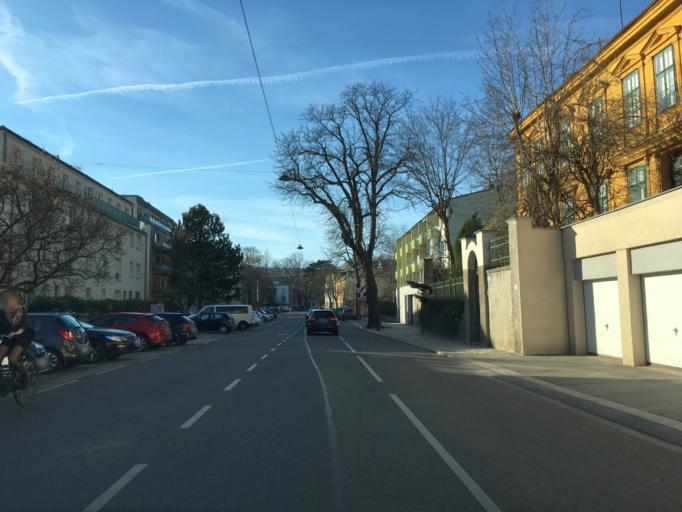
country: AT
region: Lower Austria
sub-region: Politischer Bezirk Wien-Umgebung
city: Klosterneuburg
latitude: 48.2370
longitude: 16.2878
